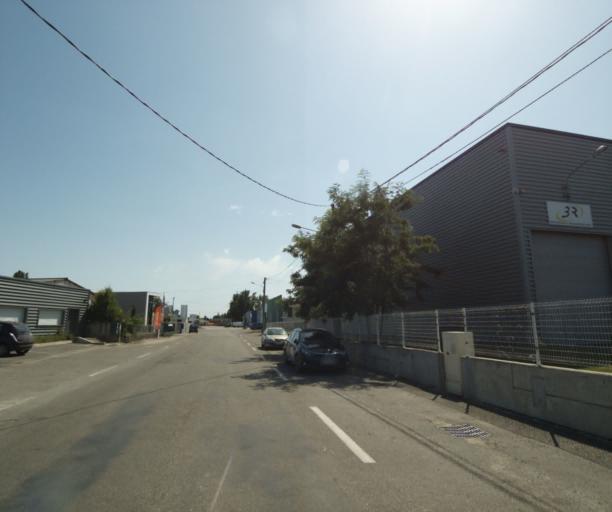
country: FR
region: Midi-Pyrenees
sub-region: Departement du Tarn-et-Garonne
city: Montauban
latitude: 44.0384
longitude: 1.3636
